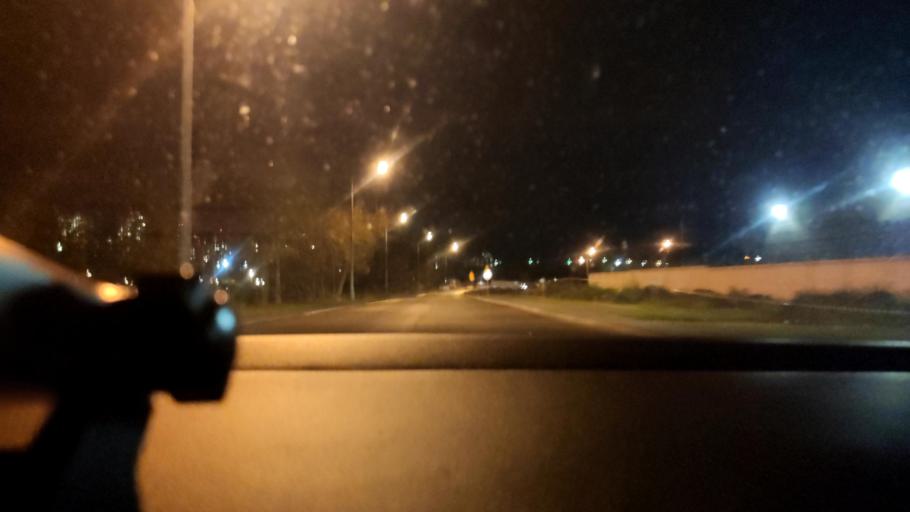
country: RU
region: Moskovskaya
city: Kur'yanovo
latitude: 55.6485
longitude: 37.6896
